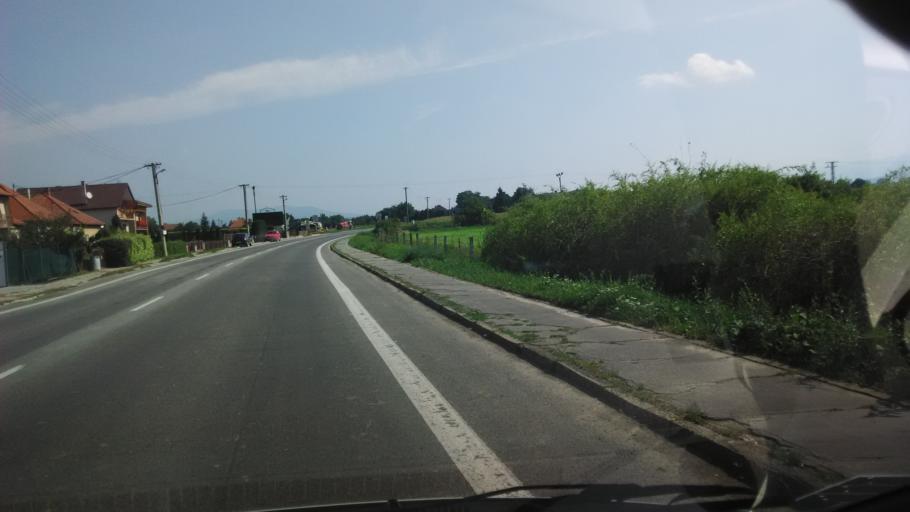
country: SK
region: Nitriansky
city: Banovce nad Bebravou
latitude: 48.6072
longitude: 18.2257
